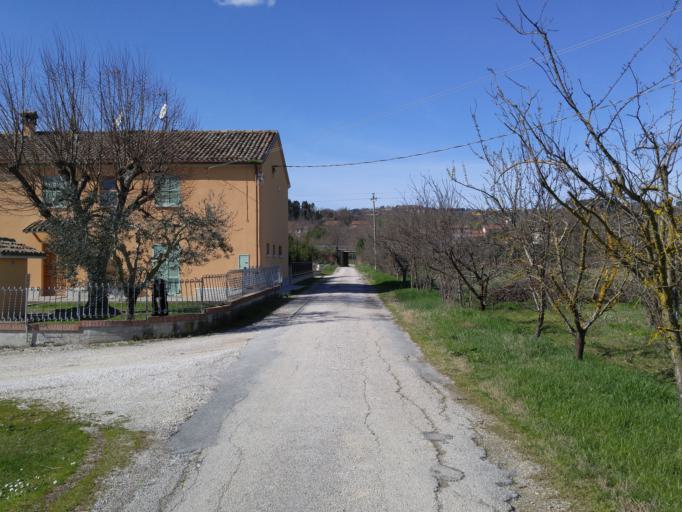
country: IT
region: The Marches
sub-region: Provincia di Pesaro e Urbino
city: Calcinelli
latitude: 43.7397
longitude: 12.9124
